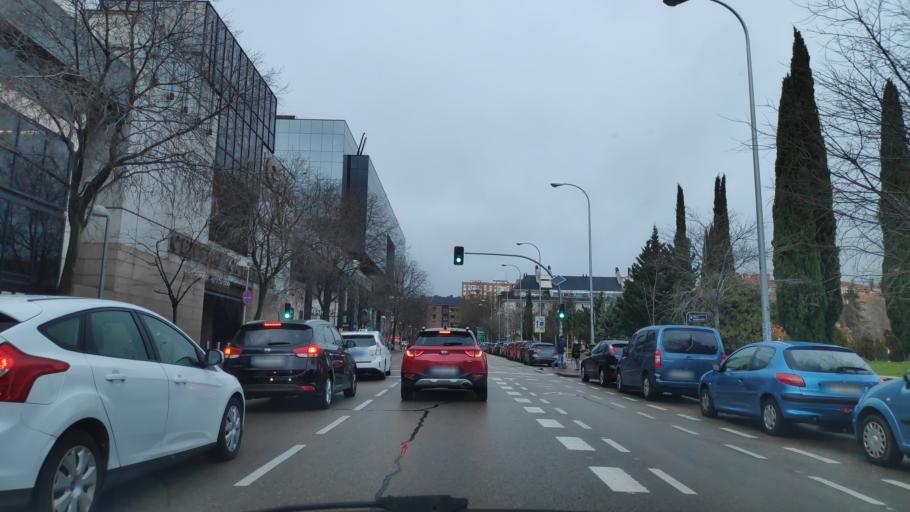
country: ES
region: Madrid
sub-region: Provincia de Madrid
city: Hortaleza
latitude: 40.4699
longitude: -3.6400
